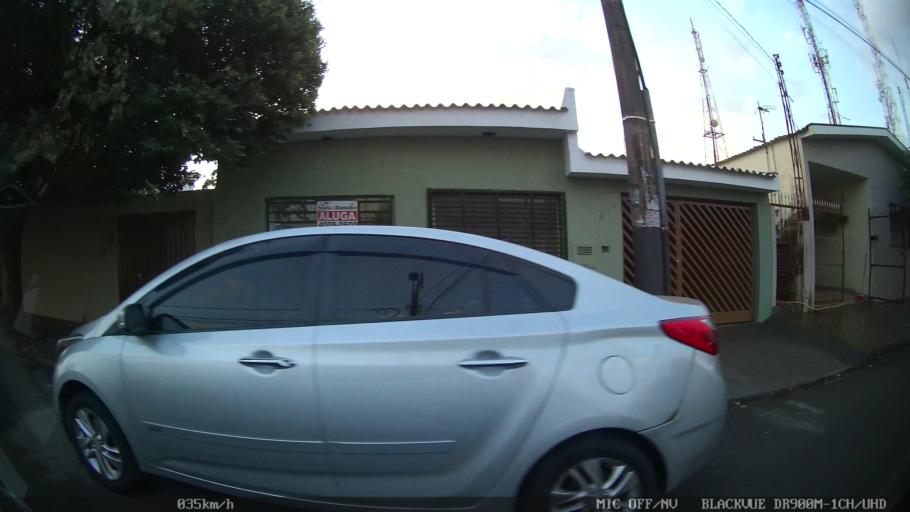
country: BR
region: Sao Paulo
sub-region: Ribeirao Preto
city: Ribeirao Preto
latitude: -21.1542
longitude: -47.8297
